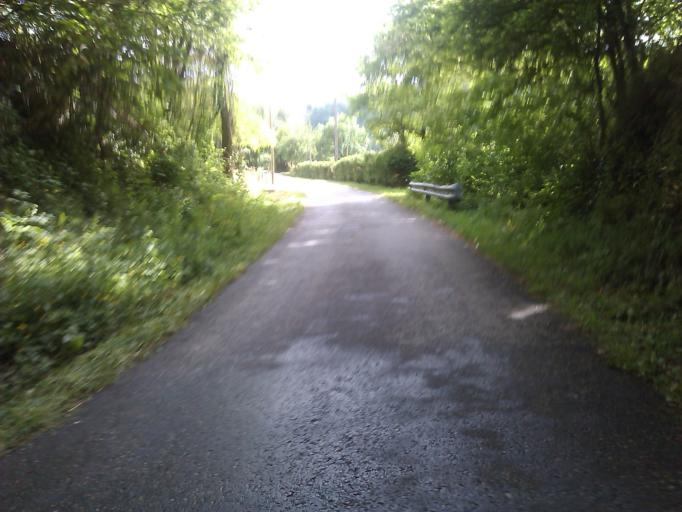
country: ES
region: Navarre
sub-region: Provincia de Navarra
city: Areso
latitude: 43.1012
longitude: -1.9448
